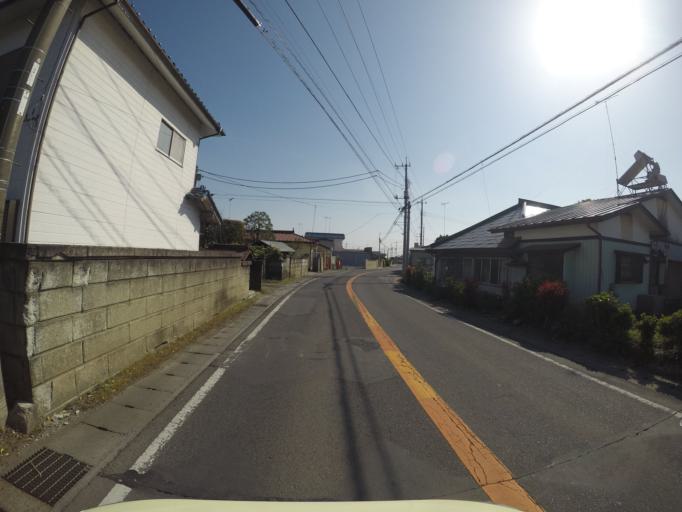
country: JP
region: Tochigi
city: Kaminokawa
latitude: 36.3720
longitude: 139.9096
